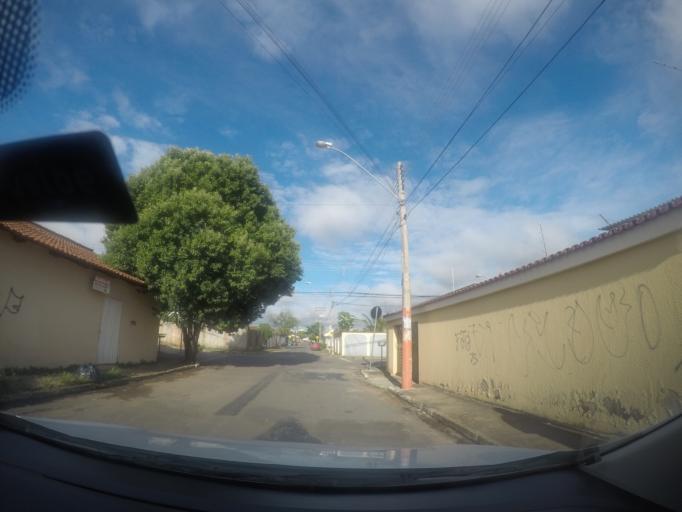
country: BR
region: Goias
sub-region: Goiania
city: Goiania
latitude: -16.6887
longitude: -49.3114
